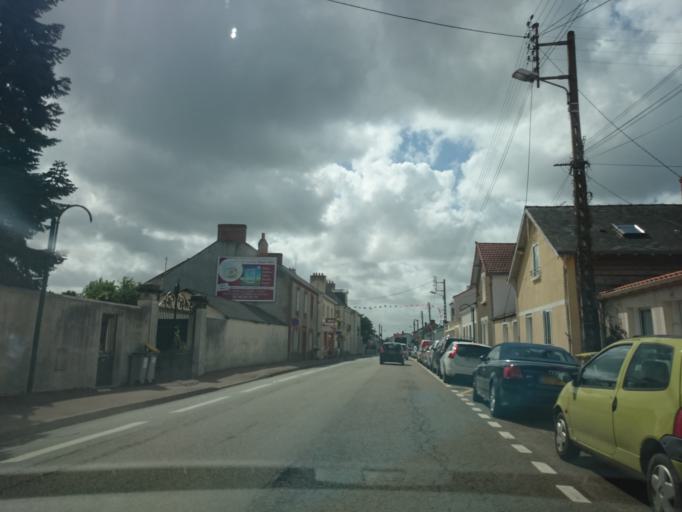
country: FR
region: Pays de la Loire
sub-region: Departement de la Loire-Atlantique
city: Bouaye
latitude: 47.1440
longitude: -1.6904
